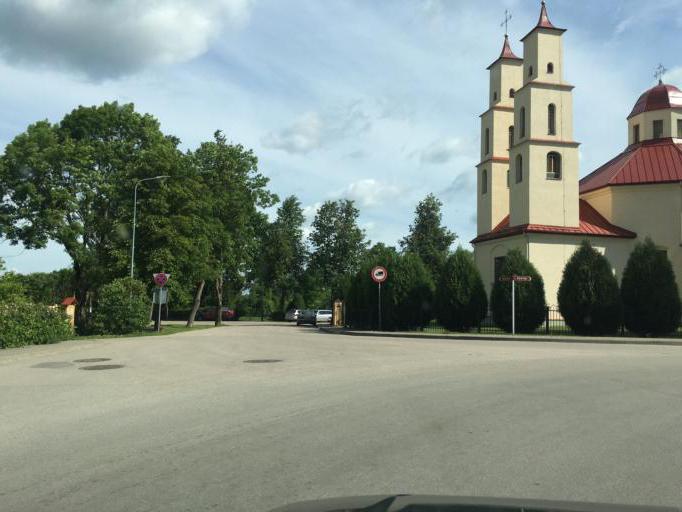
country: LV
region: Balvu Rajons
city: Balvi
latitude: 57.1333
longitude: 27.2713
